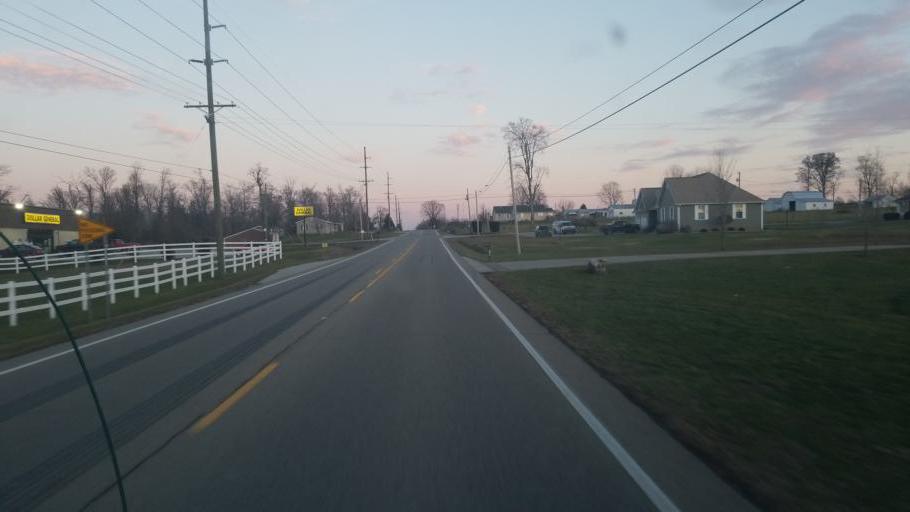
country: US
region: Indiana
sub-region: Lawrence County
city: Bedford
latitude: 38.8748
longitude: -86.3494
